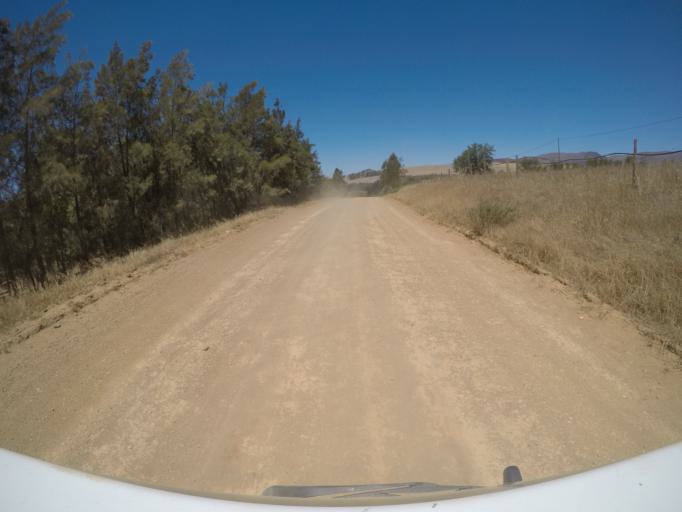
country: ZA
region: Western Cape
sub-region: Overberg District Municipality
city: Grabouw
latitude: -34.0930
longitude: 19.1963
